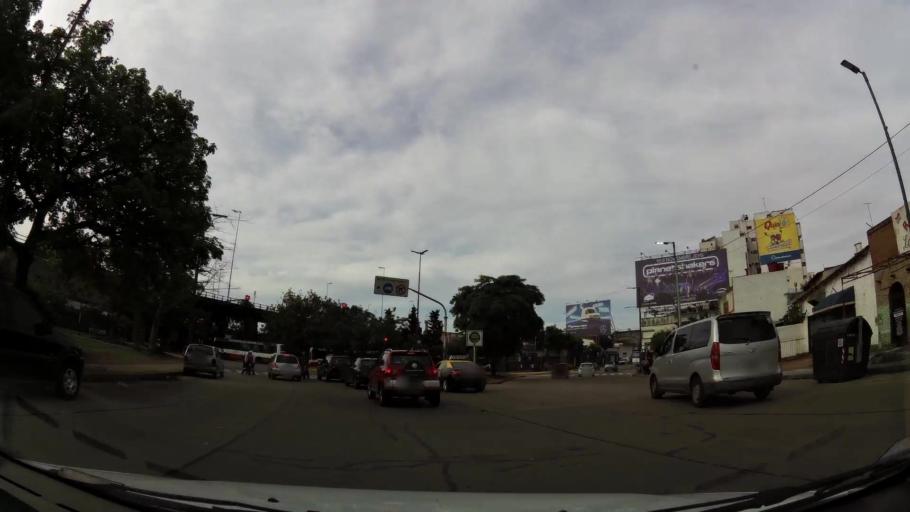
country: AR
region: Buenos Aires F.D.
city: Villa Lugano
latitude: -34.6435
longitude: -58.4609
